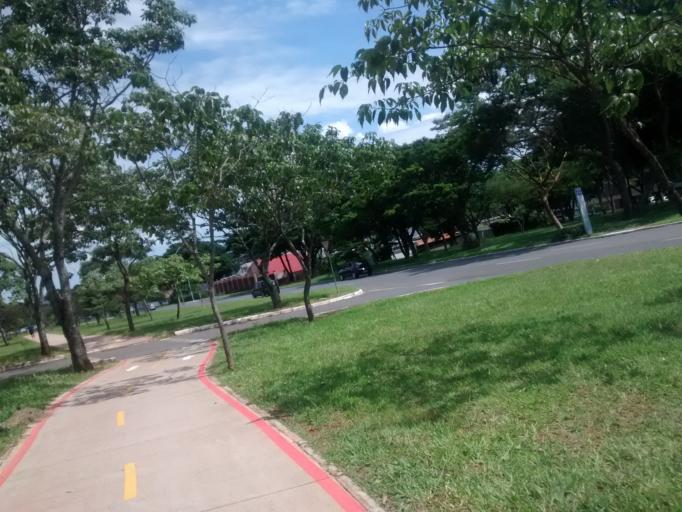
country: BR
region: Federal District
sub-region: Brasilia
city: Brasilia
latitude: -15.7613
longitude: -47.8951
